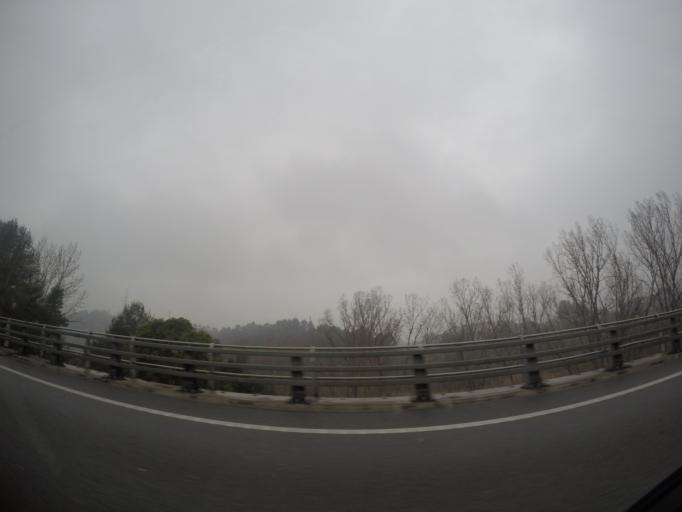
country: ES
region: Catalonia
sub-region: Provincia de Barcelona
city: Gelida
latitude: 41.4424
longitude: 1.8480
